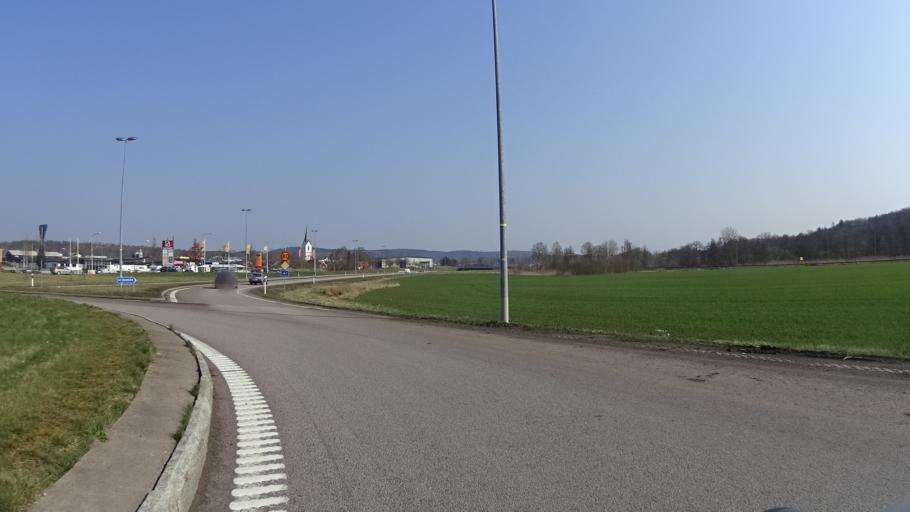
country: SE
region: Halland
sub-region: Varbergs Kommun
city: Veddige
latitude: 57.2590
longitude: 12.3269
